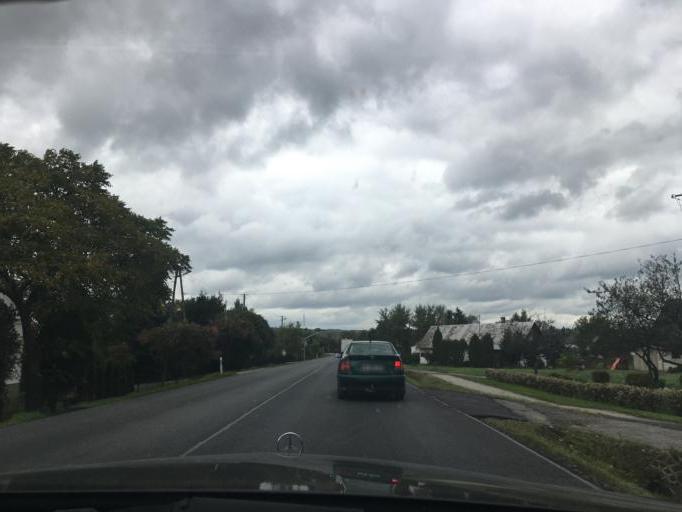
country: PL
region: Subcarpathian Voivodeship
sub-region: Powiat krosnienski
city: Kroscienko Wyzne
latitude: 49.6728
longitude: 21.8484
